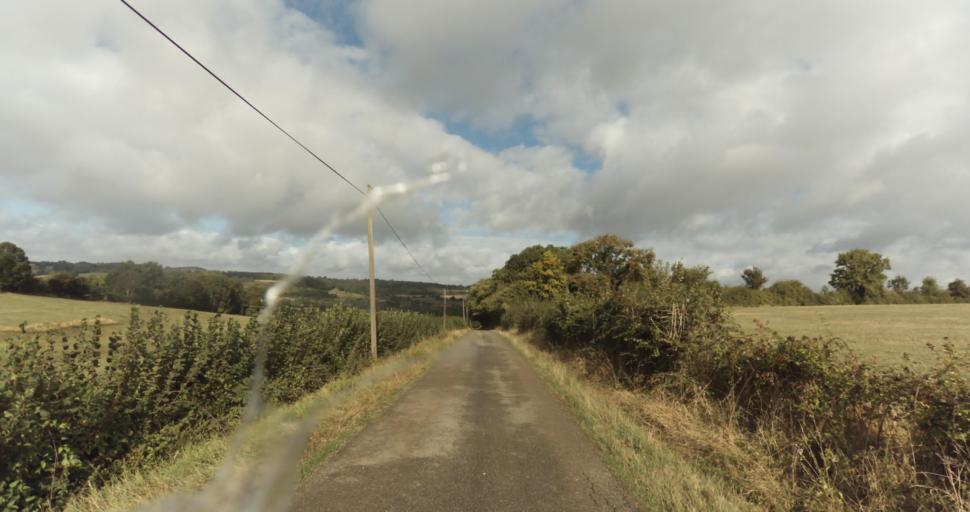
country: FR
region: Lower Normandy
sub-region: Departement de l'Orne
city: Gace
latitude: 48.8633
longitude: 0.2930
